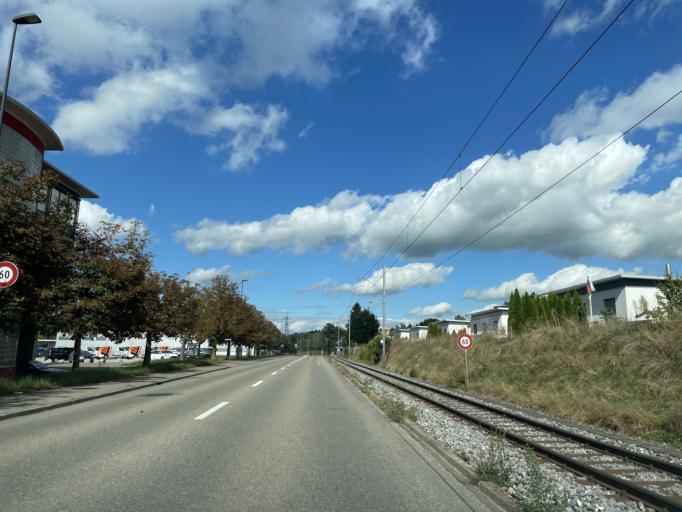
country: CH
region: Thurgau
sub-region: Muenchwilen District
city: Wangi
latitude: 47.5006
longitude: 8.9499
